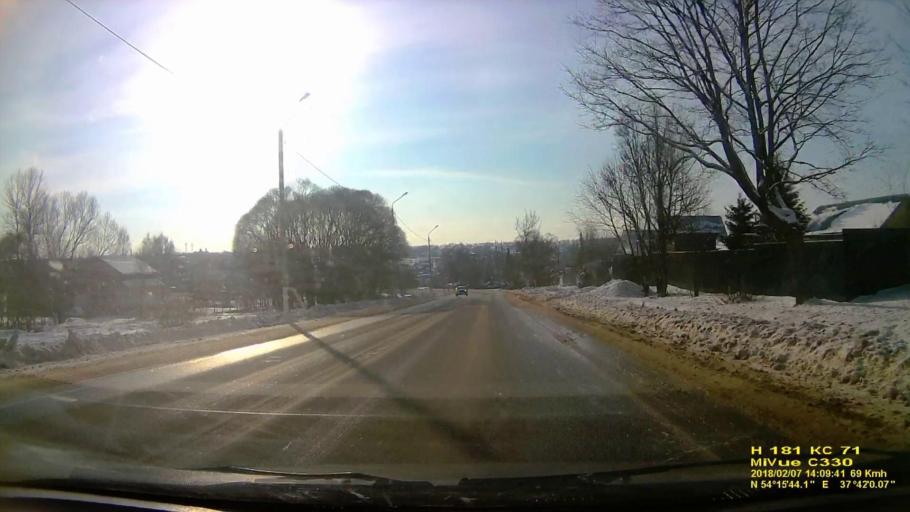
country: RU
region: Tula
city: Gorelki
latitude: 54.2622
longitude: 37.7000
